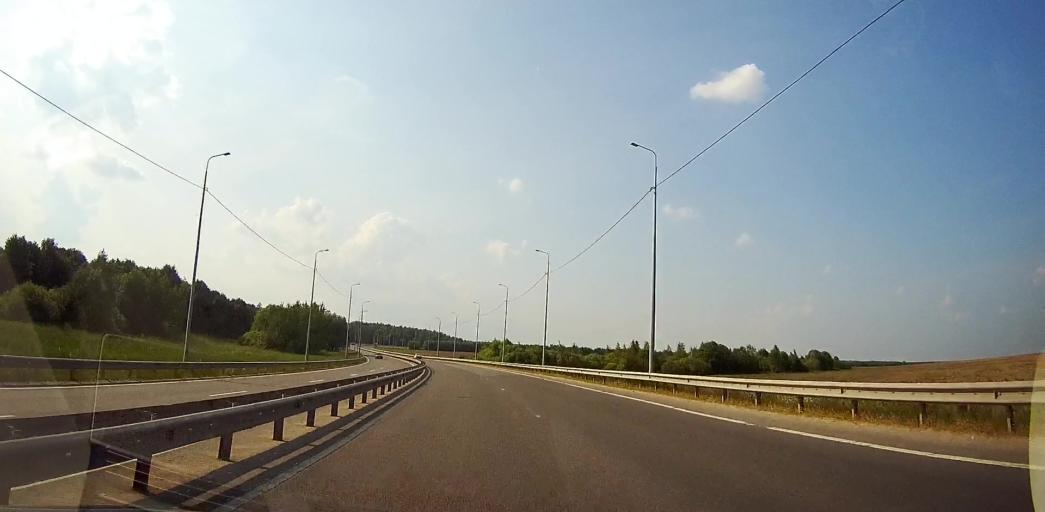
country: RU
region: Moskovskaya
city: Vostryakovo
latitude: 55.4157
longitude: 37.8566
